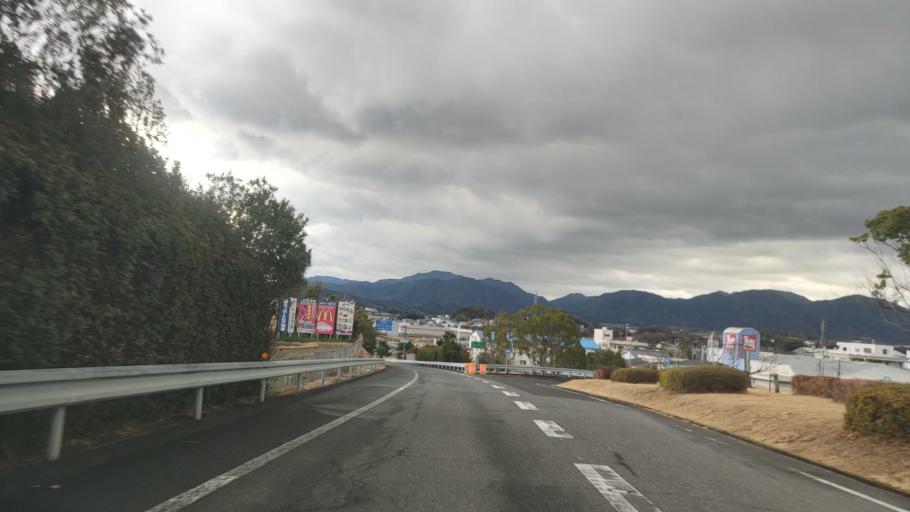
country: JP
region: Hyogo
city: Sumoto
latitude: 34.3414
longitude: 134.8475
